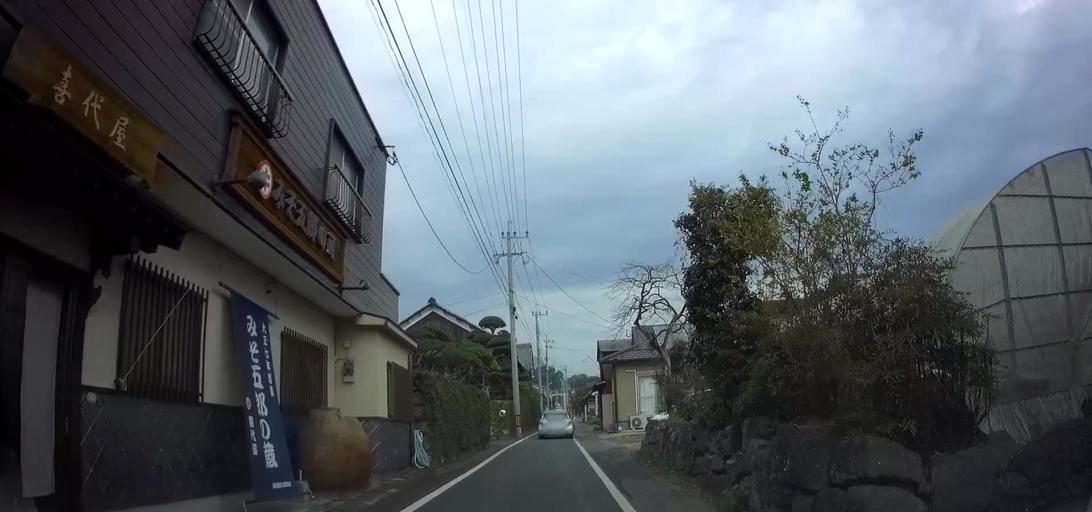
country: JP
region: Nagasaki
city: Shimabara
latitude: 32.6701
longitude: 130.3014
